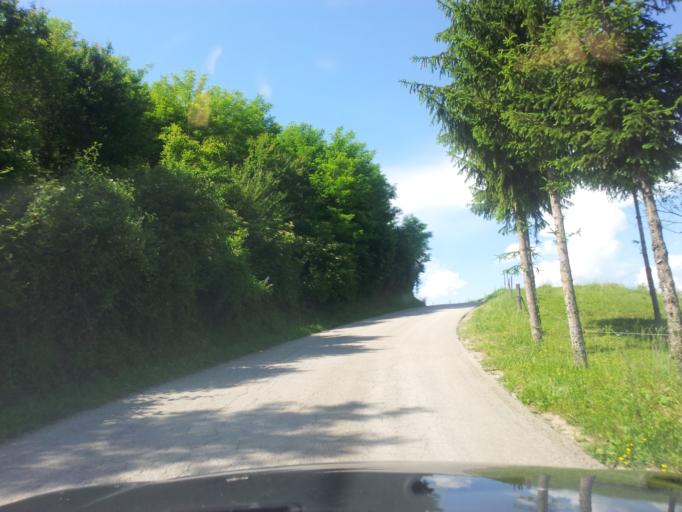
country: HR
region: Karlovacka
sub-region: Grad Karlovac
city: Karlovac
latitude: 45.4764
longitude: 15.4573
